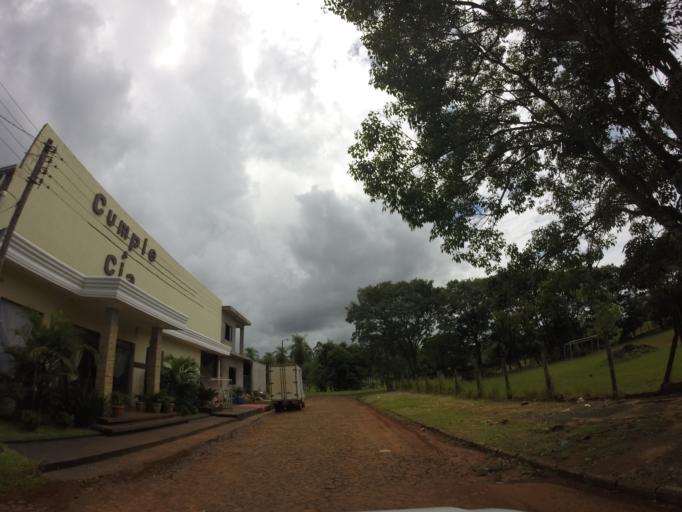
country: PY
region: Alto Parana
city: Ciudad del Este
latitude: -25.4119
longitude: -54.6278
